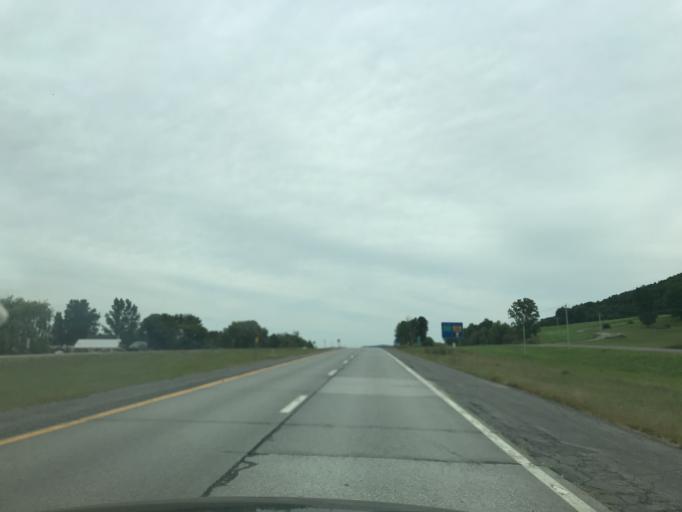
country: US
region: New York
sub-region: Schoharie County
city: Cobleskill
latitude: 42.6751
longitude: -74.4362
